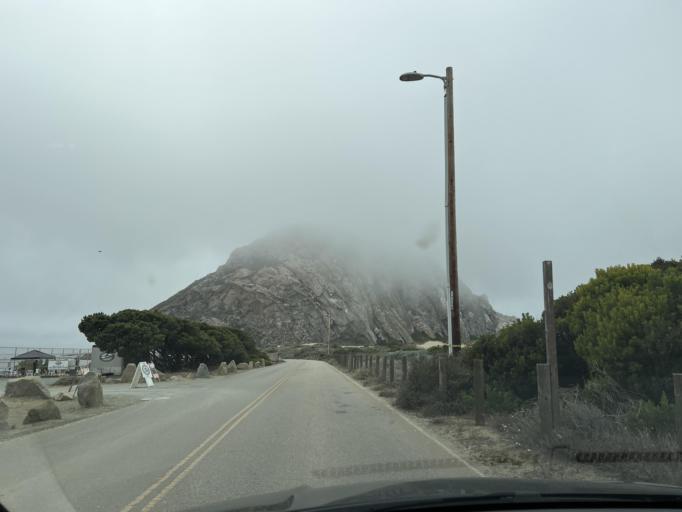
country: US
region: California
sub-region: San Luis Obispo County
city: Morro Bay
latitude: 35.3725
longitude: -120.8613
